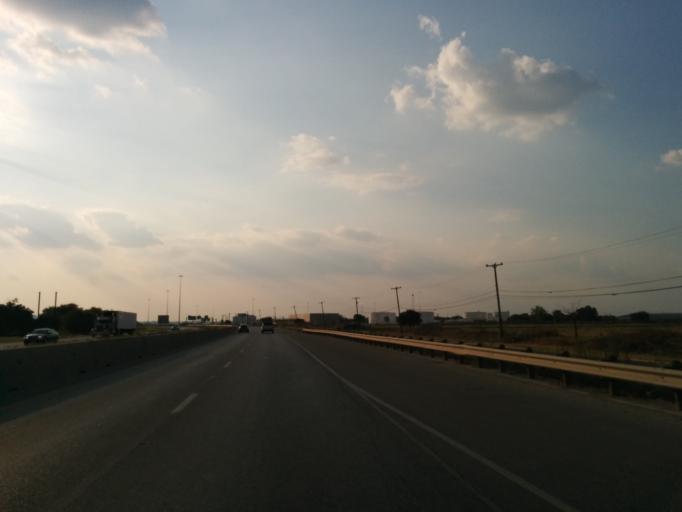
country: US
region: Texas
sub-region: Bexar County
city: Kirby
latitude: 29.4438
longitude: -98.3958
